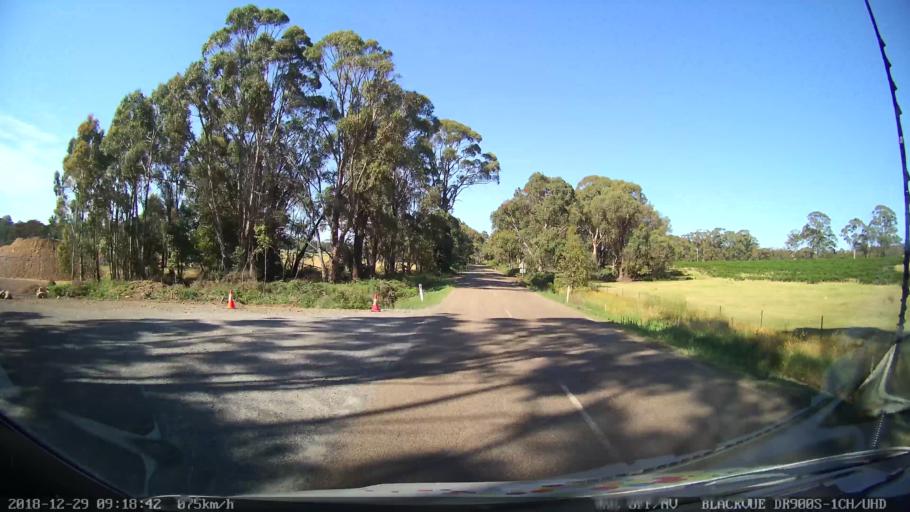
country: AU
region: New South Wales
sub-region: Upper Lachlan Shire
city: Crookwell
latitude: -34.4743
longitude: 149.4339
